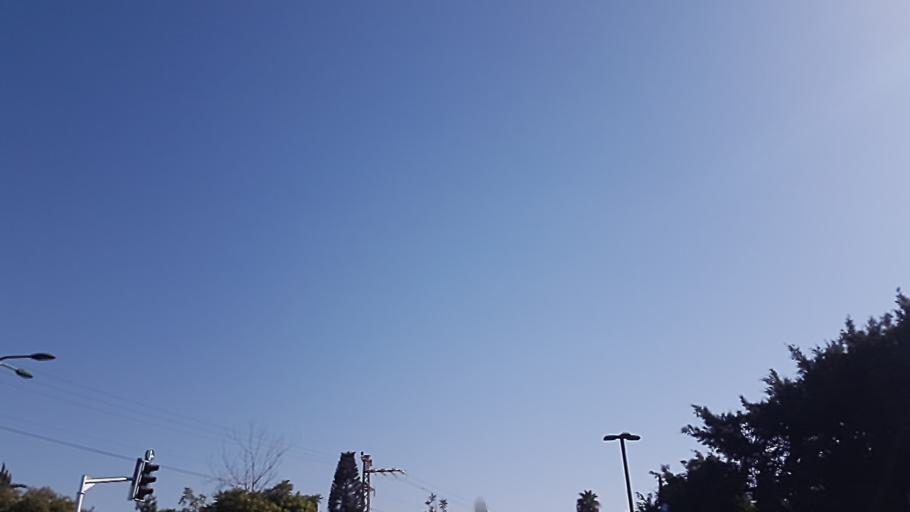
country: IL
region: Tel Aviv
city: Giv`atayim
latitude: 32.0597
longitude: 34.8212
